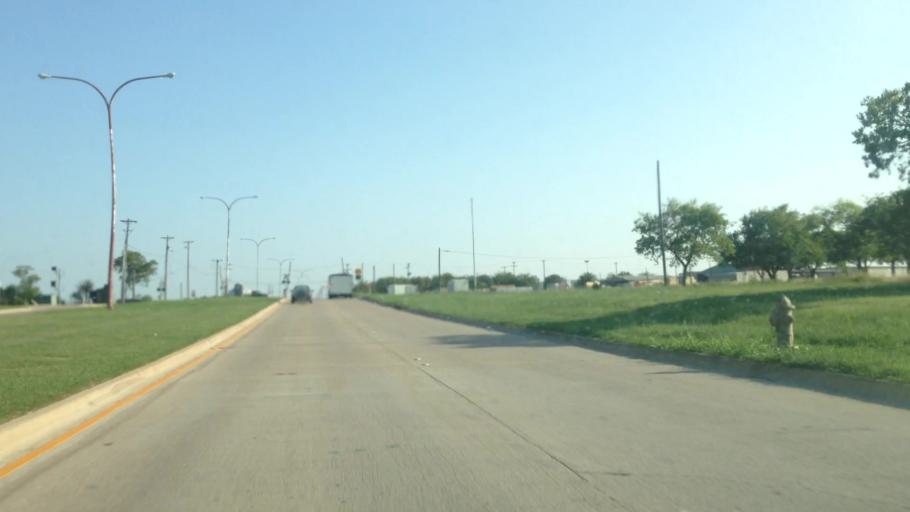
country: US
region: Texas
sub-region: Tarrant County
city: Haltom City
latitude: 32.8149
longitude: -97.3084
